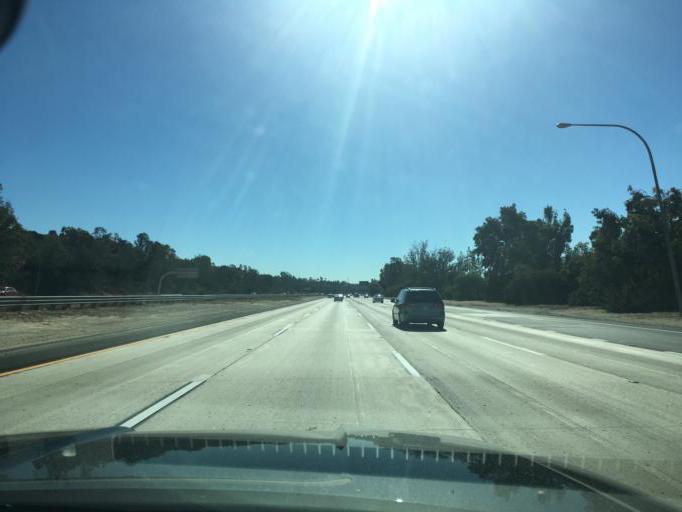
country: US
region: California
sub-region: San Diego County
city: La Mesa
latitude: 32.8193
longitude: -117.1159
